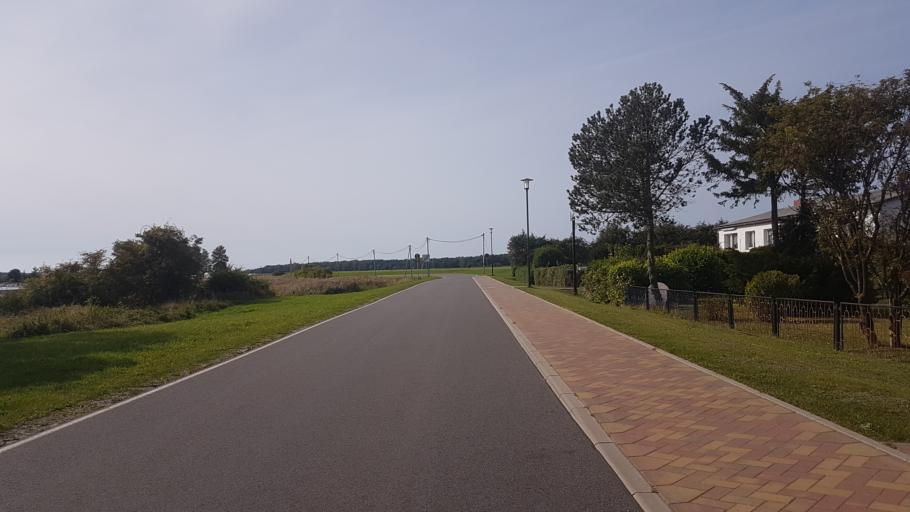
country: DE
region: Mecklenburg-Vorpommern
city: Gingst
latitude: 54.4573
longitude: 13.1756
